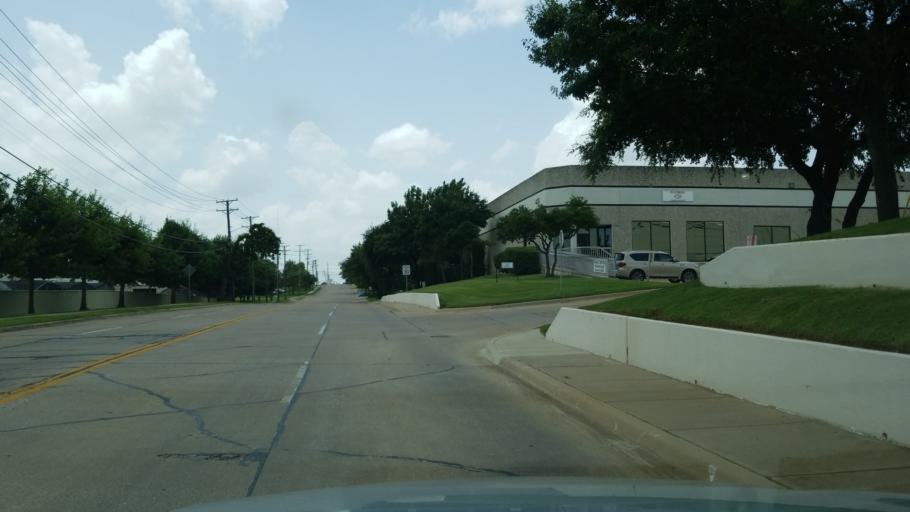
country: US
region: Texas
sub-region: Dallas County
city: Irving
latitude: 32.8236
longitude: -96.9054
